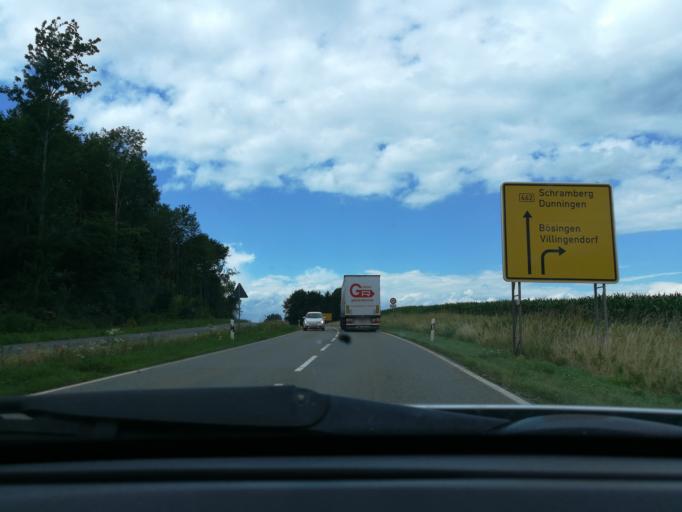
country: DE
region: Baden-Wuerttemberg
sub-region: Freiburg Region
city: Villingendorf
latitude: 48.1904
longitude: 8.5557
